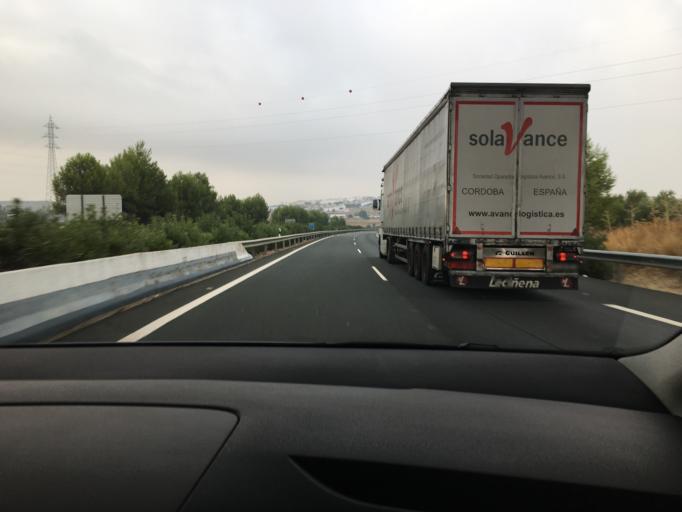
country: ES
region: Andalusia
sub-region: Province of Cordoba
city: La Carlota
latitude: 37.6859
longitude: -4.9242
